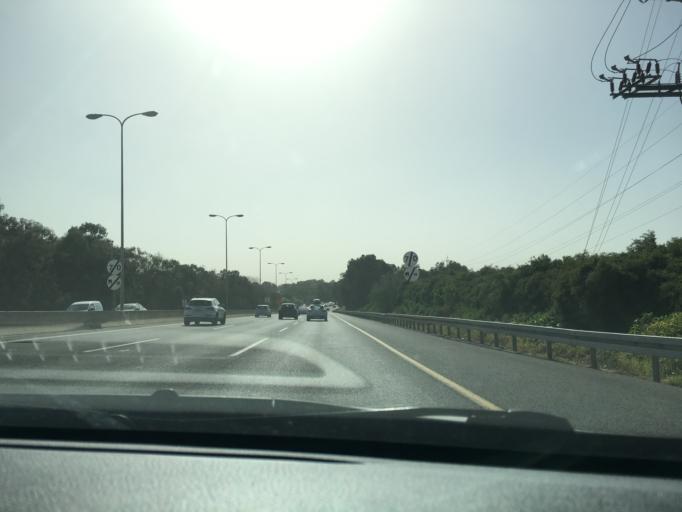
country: IL
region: Central District
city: Hod HaSharon
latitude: 32.1622
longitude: 34.8779
